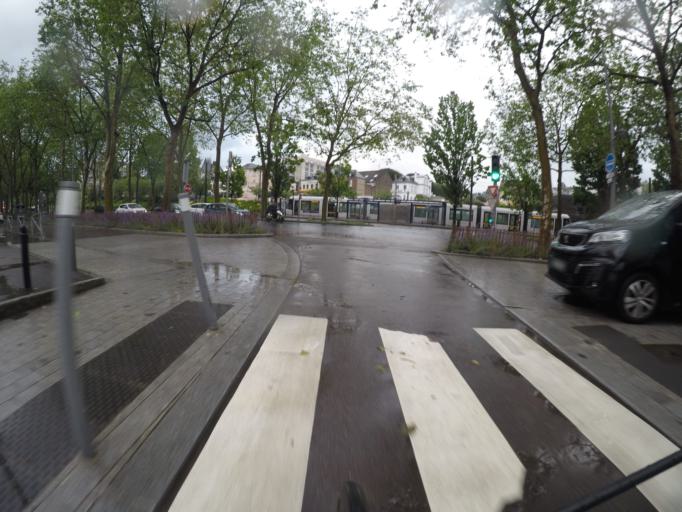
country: FR
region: Haute-Normandie
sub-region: Departement de la Seine-Maritime
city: Rouen
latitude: 49.4466
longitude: 1.1049
